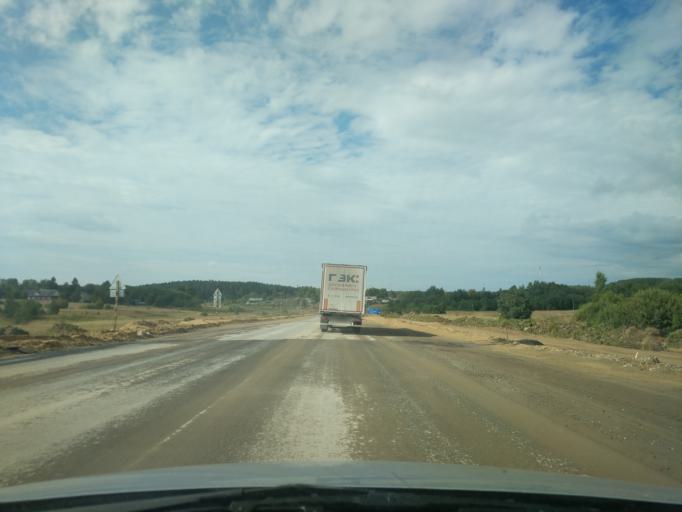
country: RU
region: Kostroma
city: Sudislavl'
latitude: 57.8743
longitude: 41.7361
